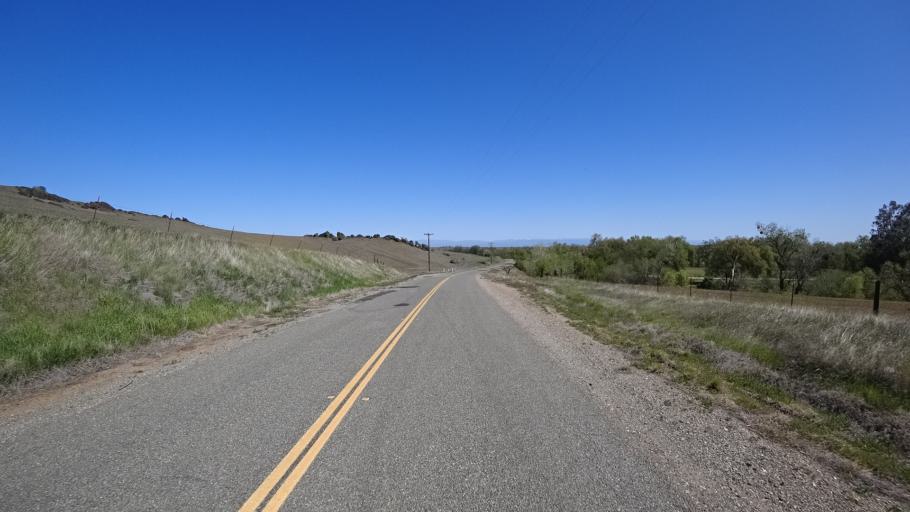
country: US
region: California
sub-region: Glenn County
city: Orland
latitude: 39.7657
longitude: -122.3308
